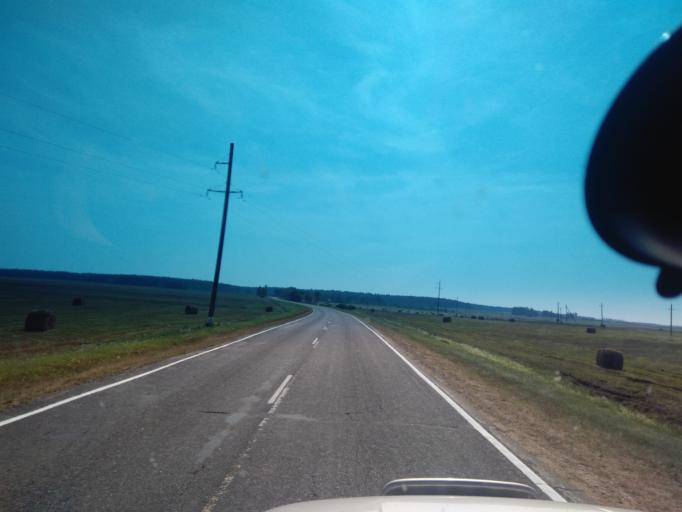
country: BY
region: Minsk
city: Uzda
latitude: 53.3956
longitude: 27.2326
